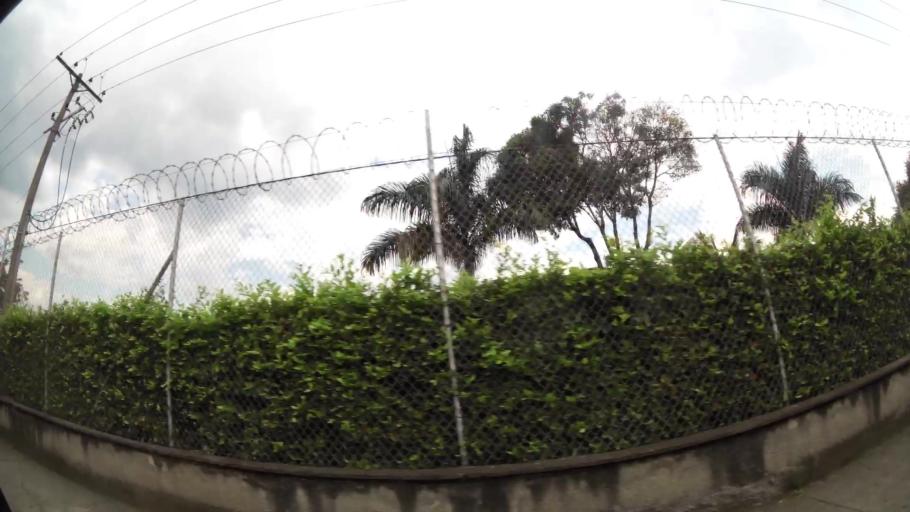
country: CO
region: Antioquia
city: Itagui
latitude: 6.1876
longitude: -75.5931
